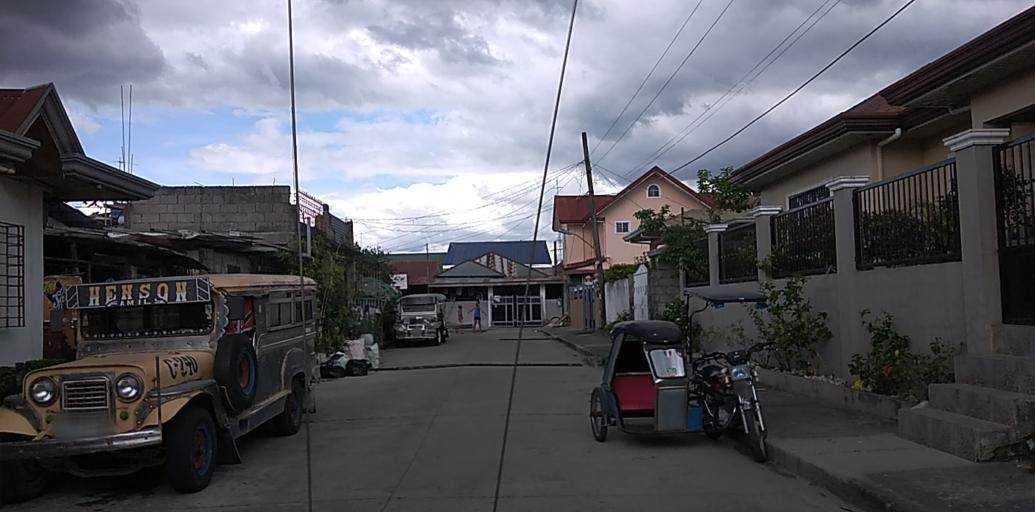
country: PH
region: Central Luzon
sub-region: Province of Pampanga
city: Pio
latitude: 15.0459
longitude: 120.5321
